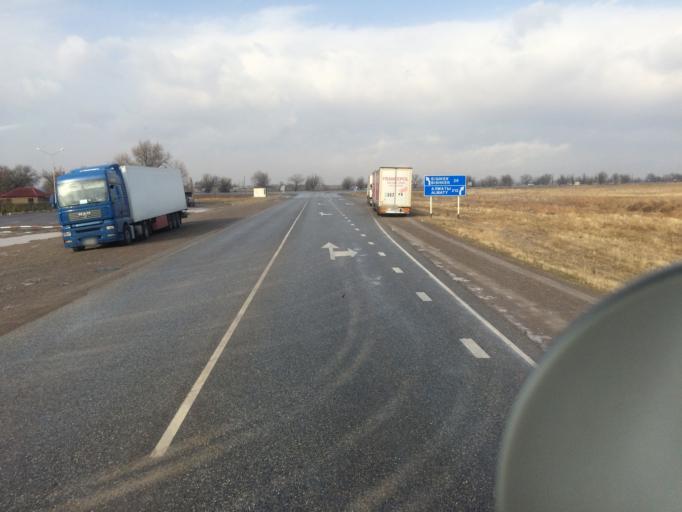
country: KZ
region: Zhambyl
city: Georgiyevka
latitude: 43.0874
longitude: 74.7083
